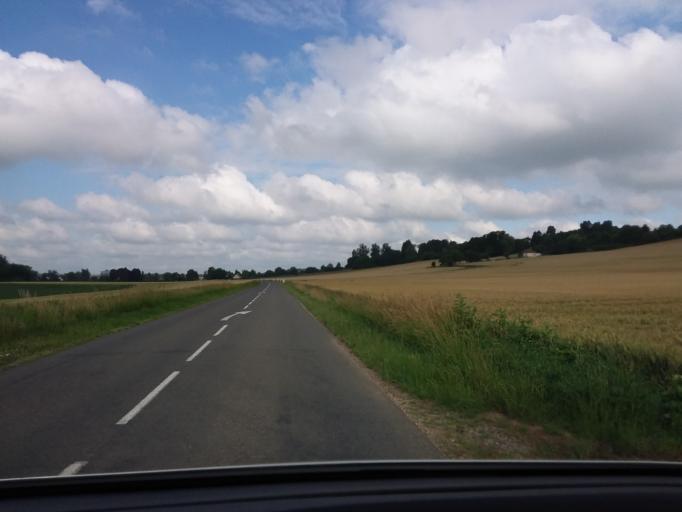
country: FR
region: Champagne-Ardenne
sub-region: Departement de la Marne
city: Fismes
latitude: 49.3883
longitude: 3.7503
